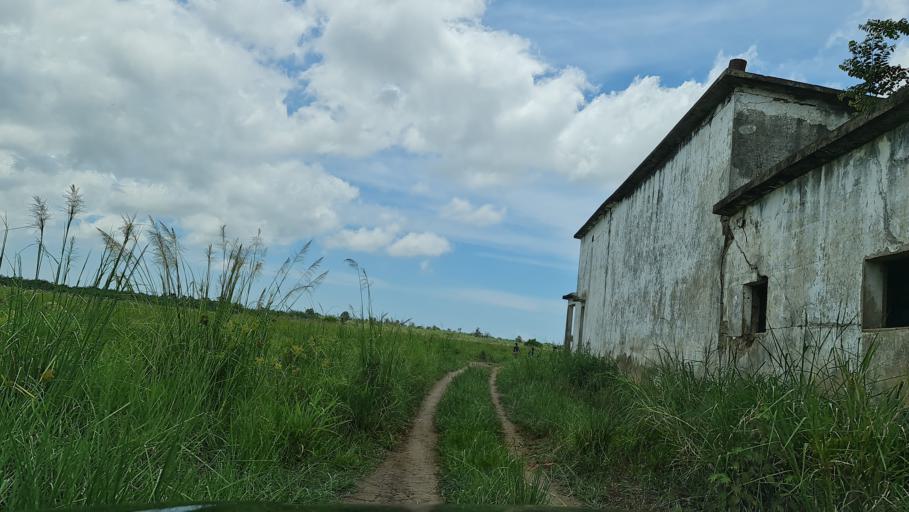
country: MZ
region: Zambezia
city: Quelimane
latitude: -17.5855
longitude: 37.3941
